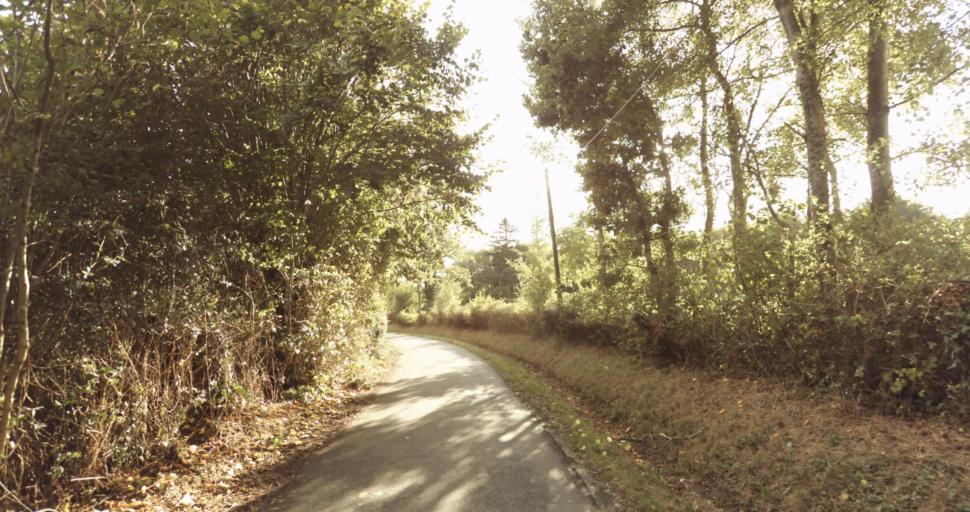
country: FR
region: Lower Normandy
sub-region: Departement de l'Orne
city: Sainte-Gauburge-Sainte-Colombe
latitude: 48.7179
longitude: 0.4112
